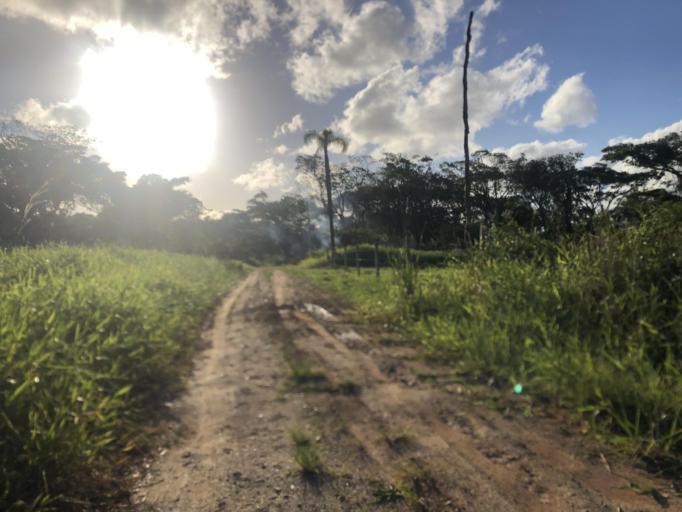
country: BR
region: Santa Catarina
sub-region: Sao Francisco Do Sul
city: Sao Francisco do Sul
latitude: -26.2182
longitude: -48.5361
